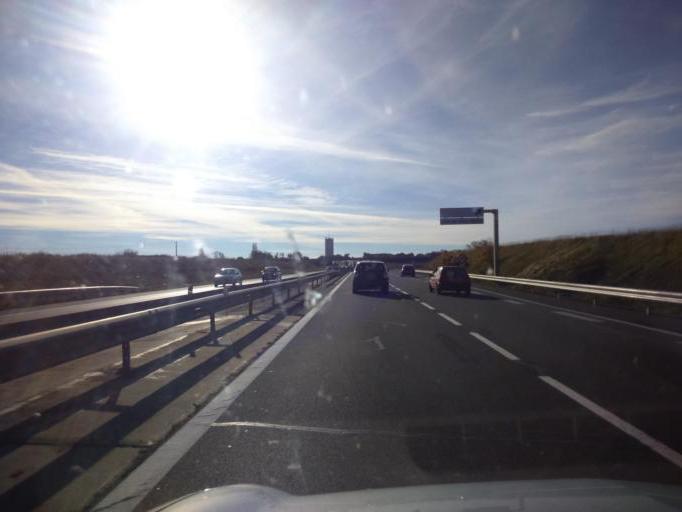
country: FR
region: Poitou-Charentes
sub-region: Departement de la Charente-Maritime
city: Aytre
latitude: 46.1457
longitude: -1.1091
